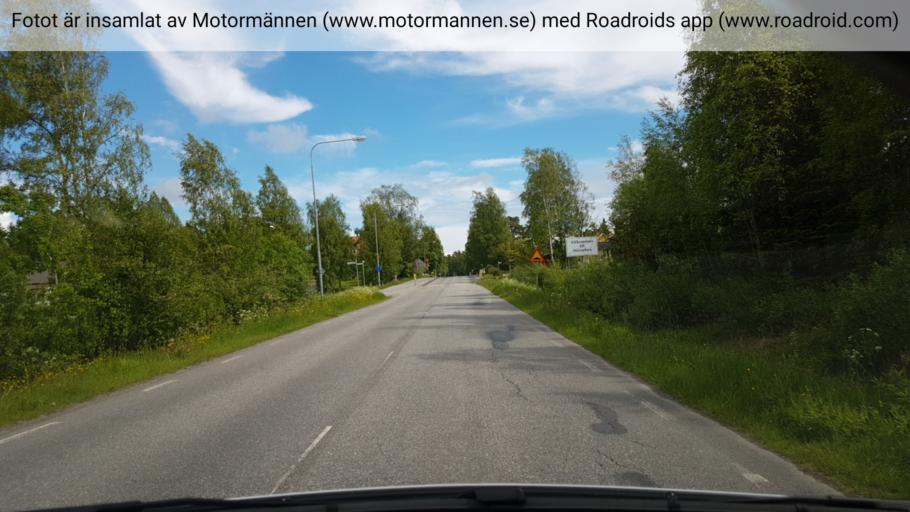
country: SE
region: Vaesterbotten
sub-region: Umea Kommun
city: Hoernefors
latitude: 63.6227
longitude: 19.8984
